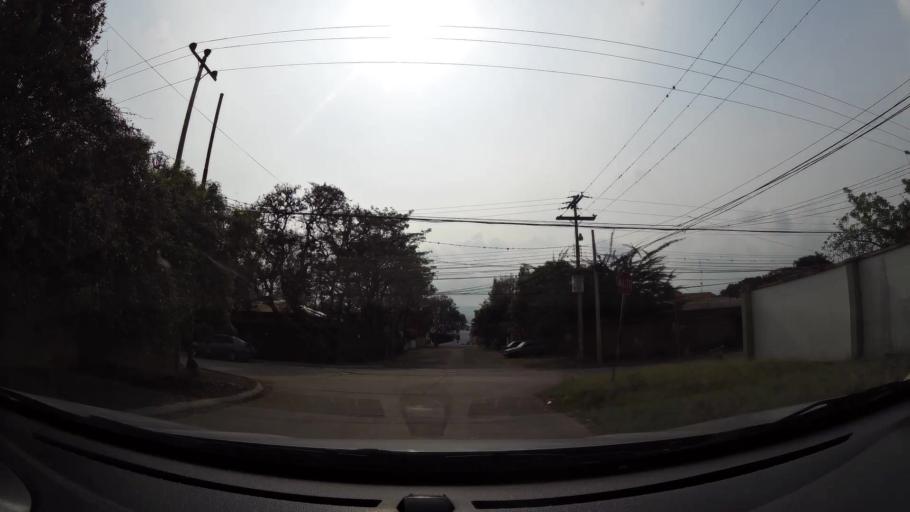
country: HN
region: Francisco Morazan
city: Tegucigalpa
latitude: 14.1047
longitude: -87.1799
